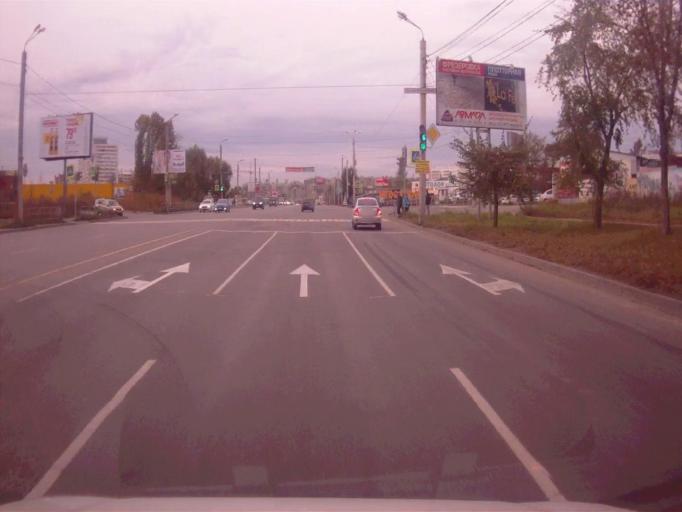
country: RU
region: Chelyabinsk
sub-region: Gorod Chelyabinsk
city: Chelyabinsk
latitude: 55.1750
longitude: 61.3809
